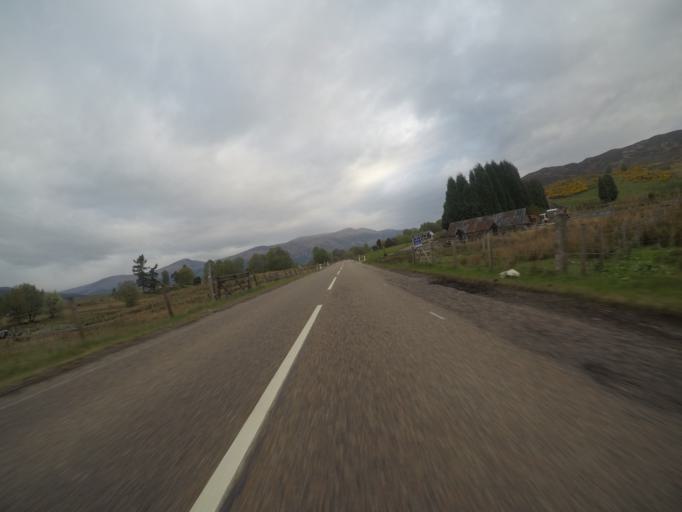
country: GB
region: Scotland
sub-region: Highland
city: Spean Bridge
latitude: 56.9142
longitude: -4.9460
